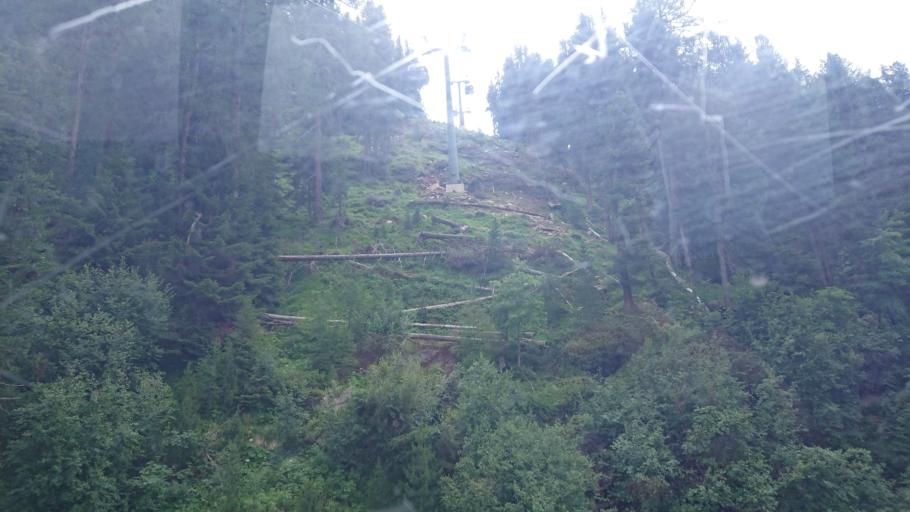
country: AT
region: Tyrol
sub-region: Politischer Bezirk Imst
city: Oetz
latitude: 47.2203
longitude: 10.9323
